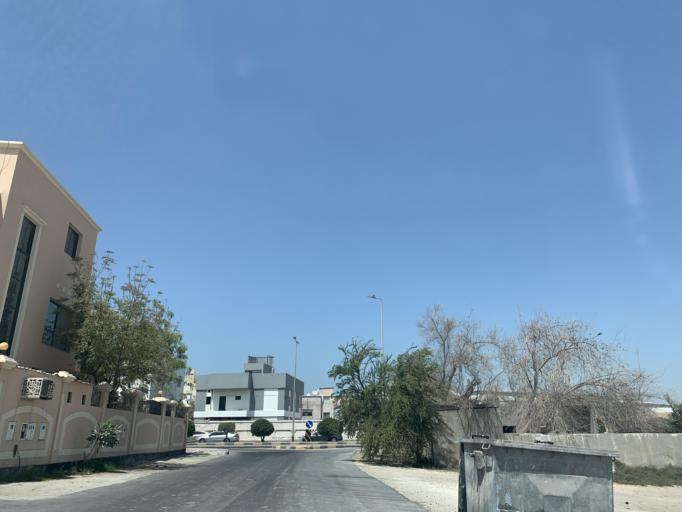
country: BH
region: Manama
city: Manama
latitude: 26.2122
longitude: 50.5688
